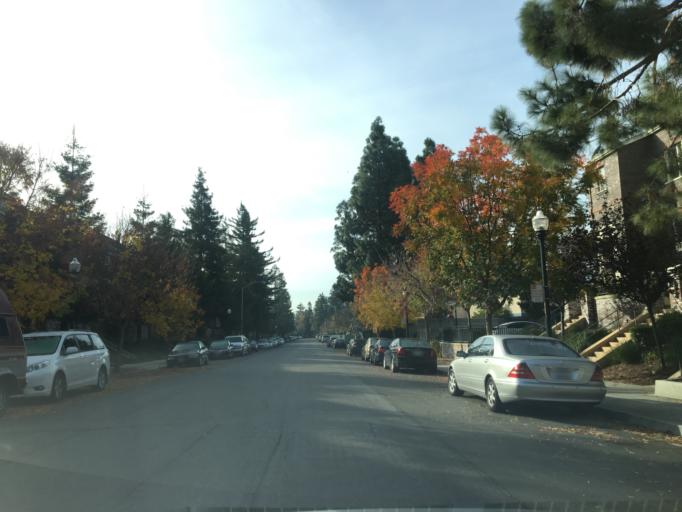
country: US
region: California
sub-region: Santa Clara County
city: Sunnyvale
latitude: 37.4031
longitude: -122.0129
